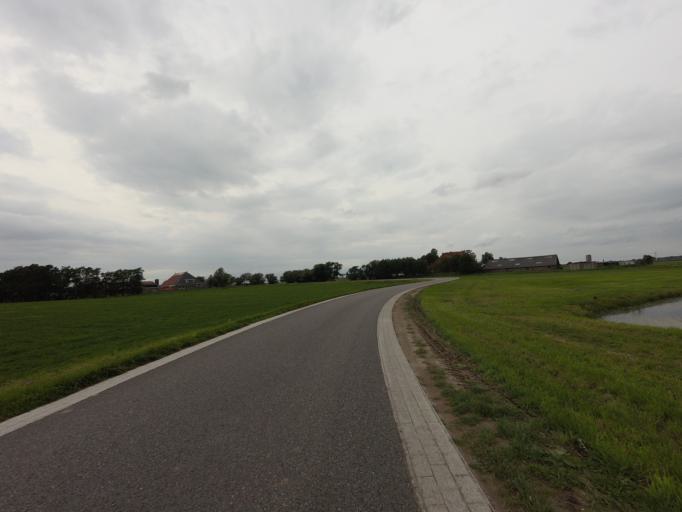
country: NL
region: Friesland
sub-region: Sudwest Fryslan
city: Bolsward
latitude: 53.0253
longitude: 5.5246
